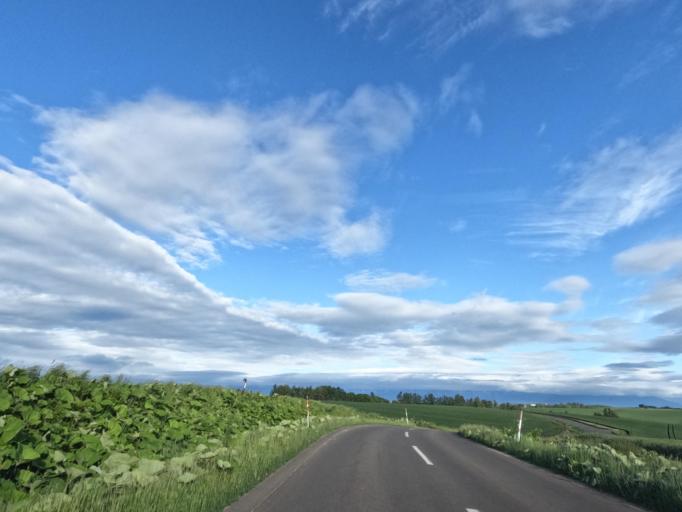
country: JP
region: Hokkaido
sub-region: Asahikawa-shi
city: Asahikawa
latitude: 43.6258
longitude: 142.4373
